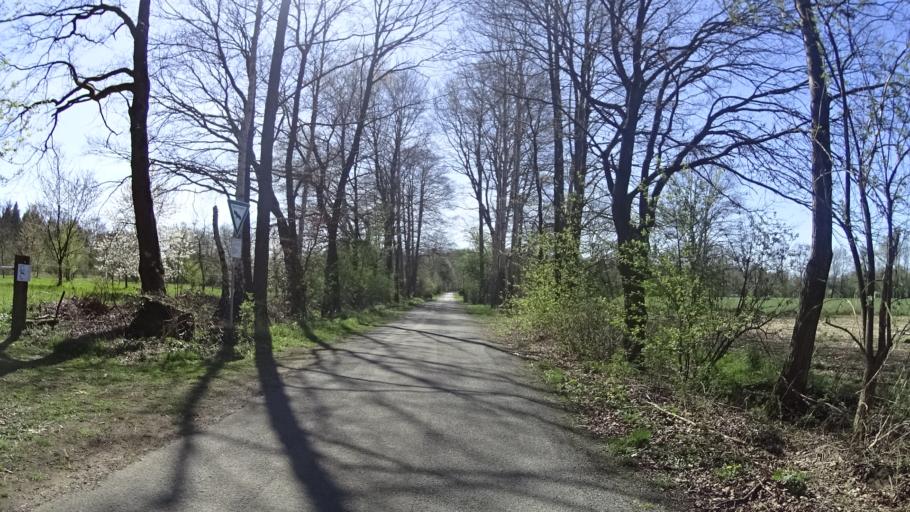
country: DE
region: North Rhine-Westphalia
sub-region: Regierungsbezirk Munster
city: Haltern
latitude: 51.7766
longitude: 7.2393
